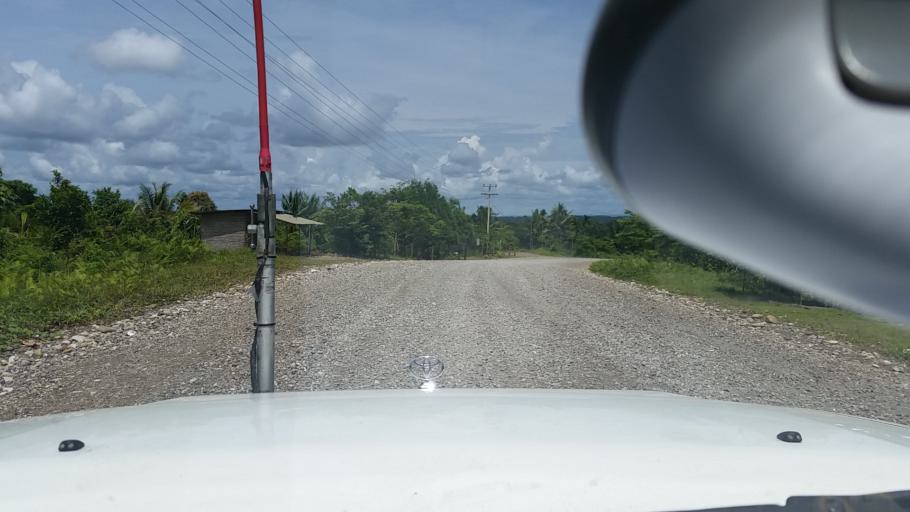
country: PG
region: Western Province
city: Kiunga
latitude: -5.6868
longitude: 141.1491
